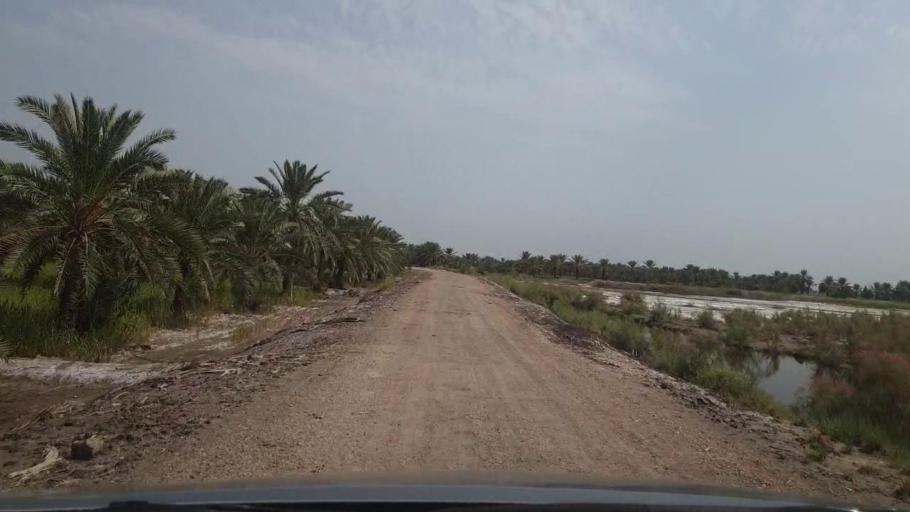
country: PK
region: Sindh
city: Rohri
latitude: 27.6783
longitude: 69.0352
